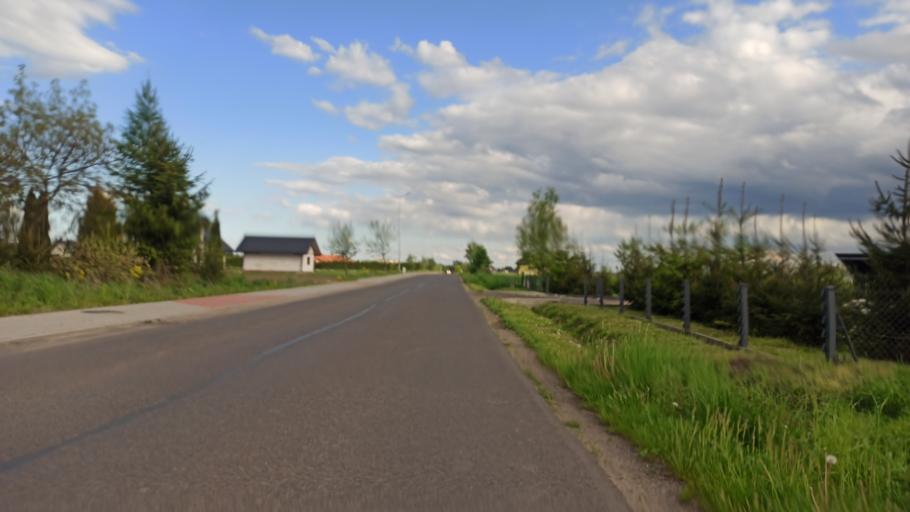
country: PL
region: Subcarpathian Voivodeship
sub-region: Powiat jaroslawski
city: Radymno
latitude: 49.9265
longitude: 22.8471
